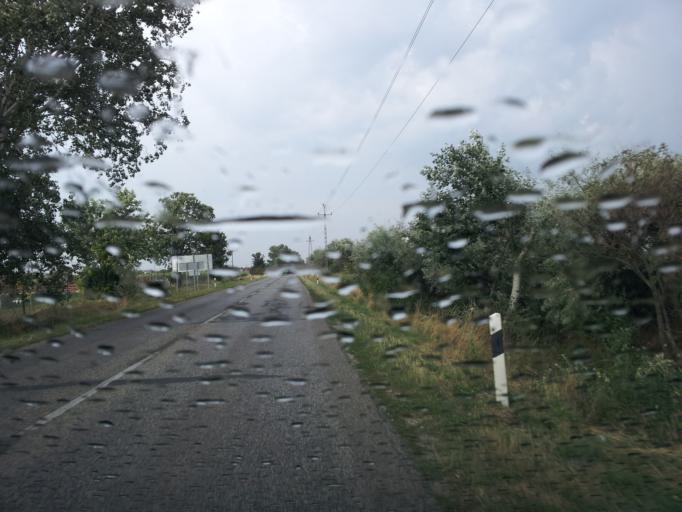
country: HU
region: Pest
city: Taksony
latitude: 47.3156
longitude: 19.0433
